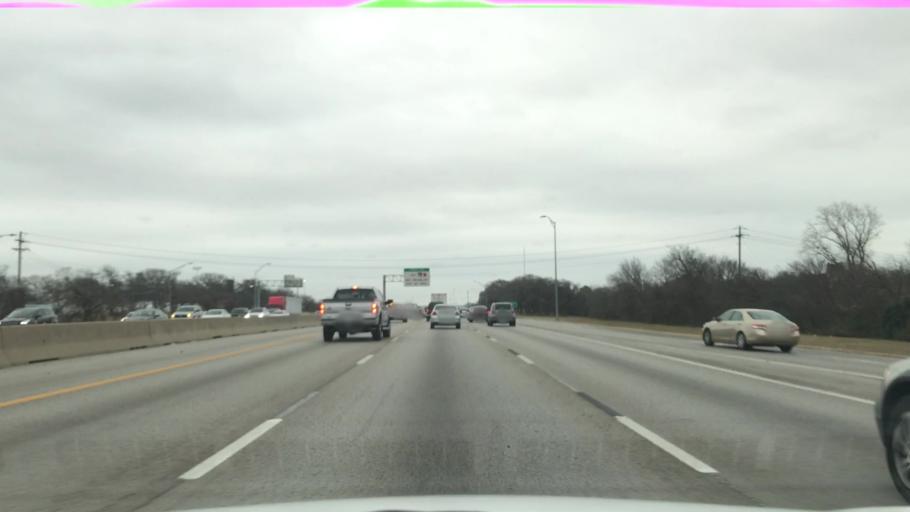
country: US
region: Texas
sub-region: Tarrant County
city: Arlington
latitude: 32.7597
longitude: -97.1295
